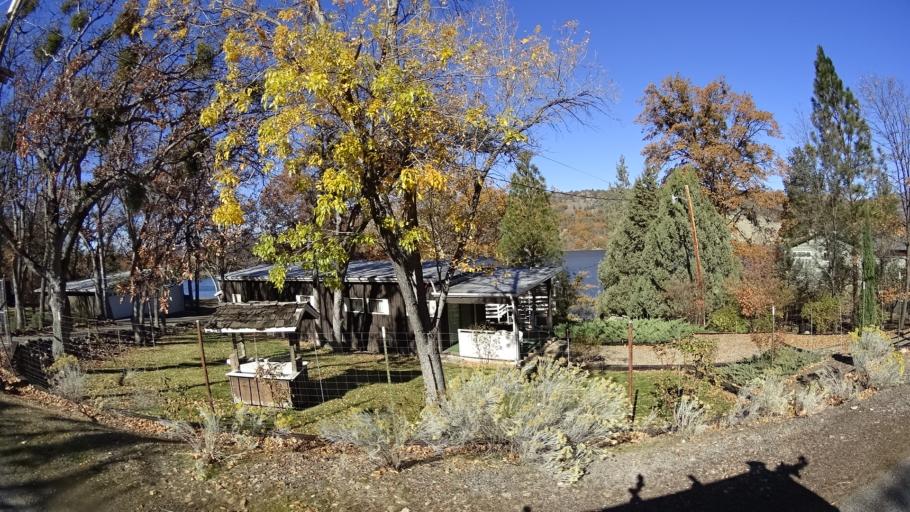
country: US
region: California
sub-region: Siskiyou County
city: Montague
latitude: 41.9792
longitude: -122.3163
